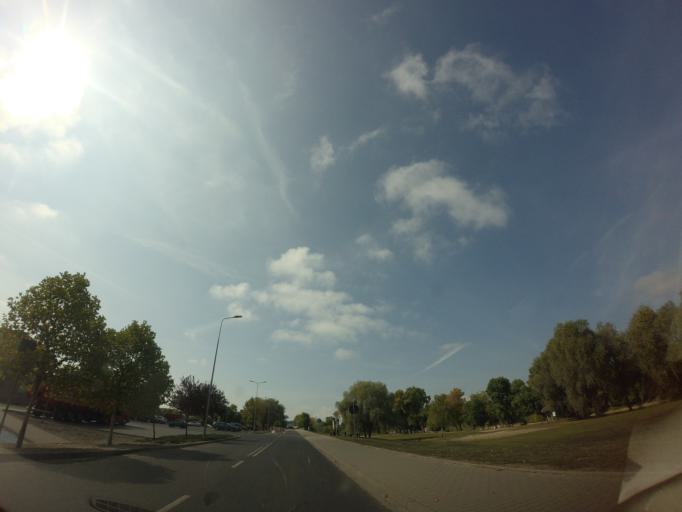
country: PL
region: Greater Poland Voivodeship
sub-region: Powiat miedzychodzki
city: Miedzychod
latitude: 52.6055
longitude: 15.8920
